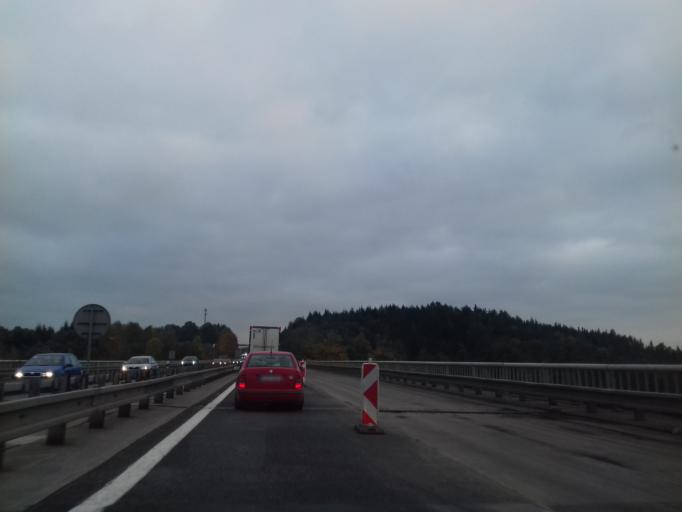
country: CZ
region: Central Bohemia
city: Ondrejov
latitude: 49.9006
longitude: 14.7396
